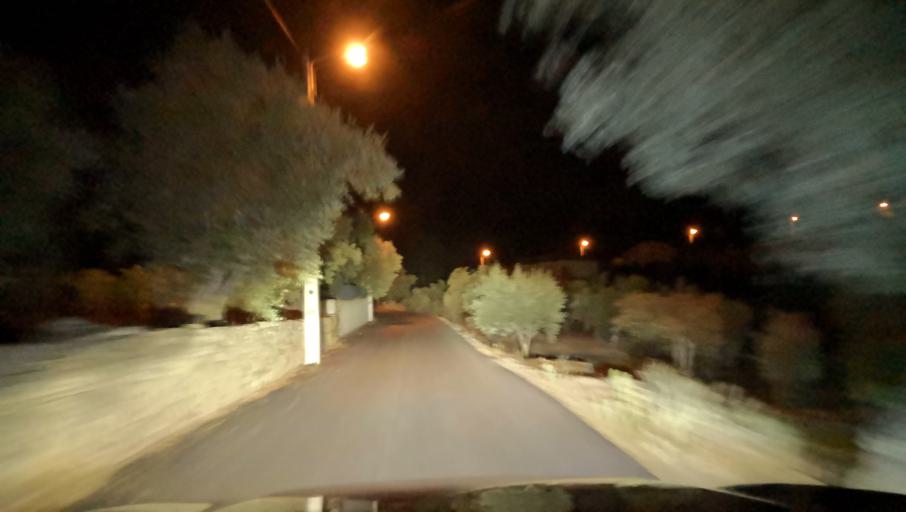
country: PT
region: Vila Real
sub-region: Sabrosa
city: Vilela
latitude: 41.2119
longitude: -7.6883
